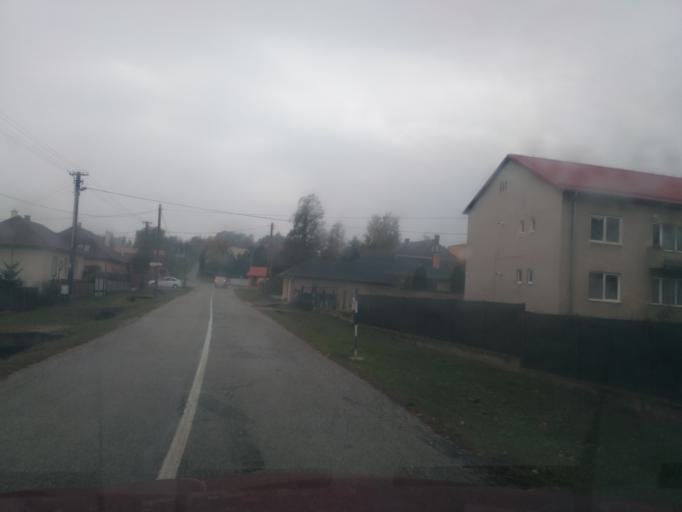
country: SK
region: Kosicky
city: Moldava nad Bodvou
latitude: 48.6751
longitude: 21.1154
